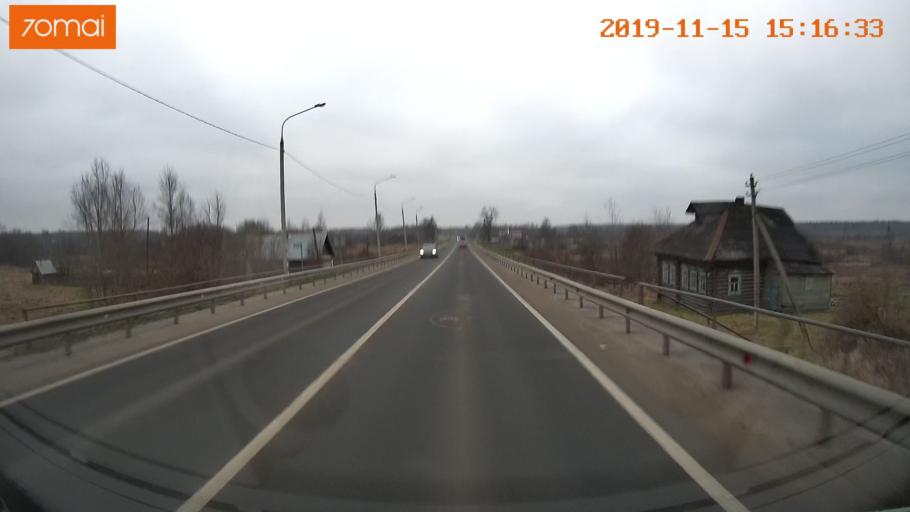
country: RU
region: Jaroslavl
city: Danilov
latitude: 58.2720
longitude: 40.1901
